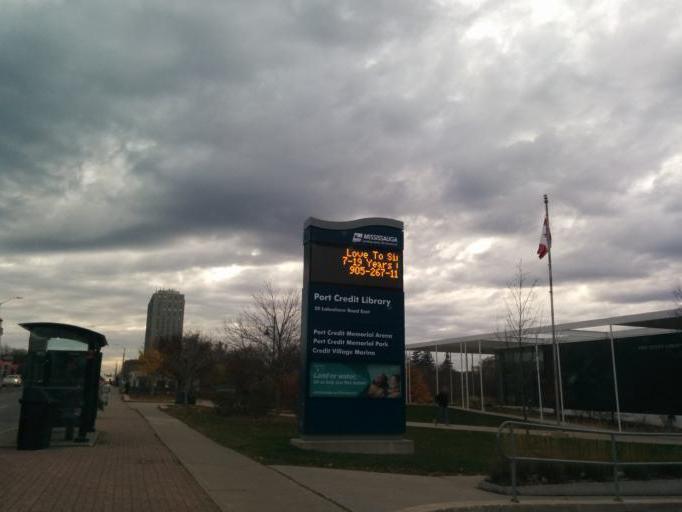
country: CA
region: Ontario
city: Mississauga
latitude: 43.5516
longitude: -79.5858
